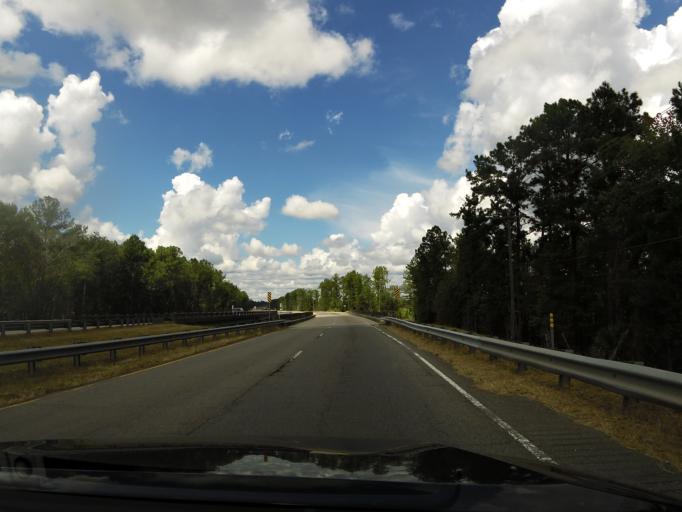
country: US
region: Georgia
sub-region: Charlton County
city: Folkston
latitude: 30.7968
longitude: -81.9855
